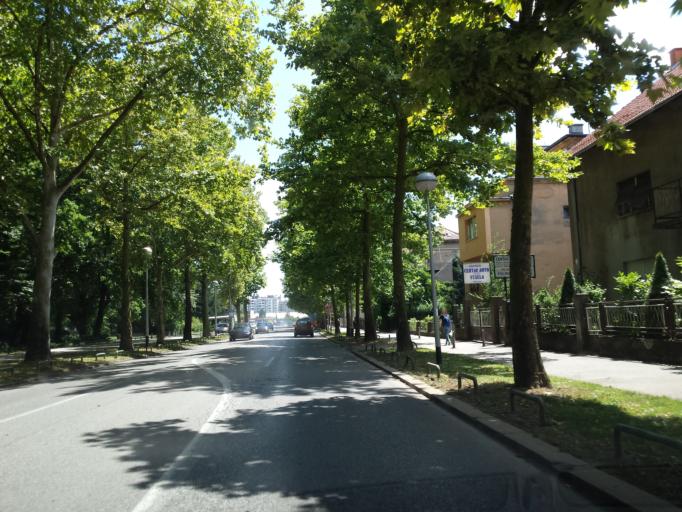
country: HR
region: Grad Zagreb
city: Zagreb
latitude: 45.8208
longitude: 16.0126
